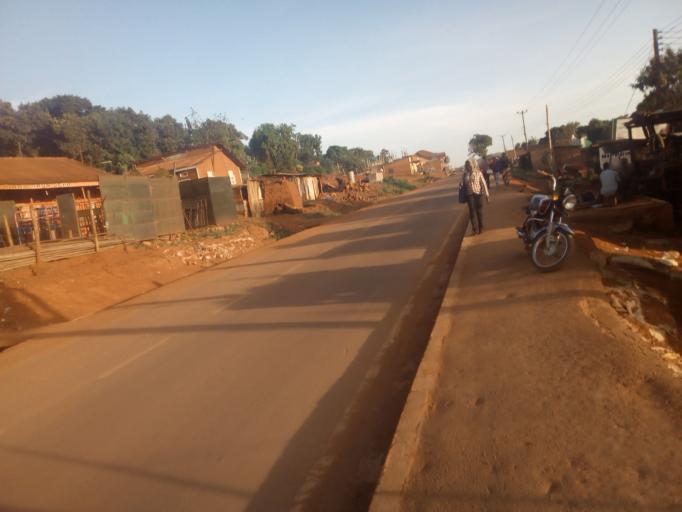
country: UG
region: Central Region
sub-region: Wakiso District
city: Kajansi
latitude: 0.2509
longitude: 32.5704
